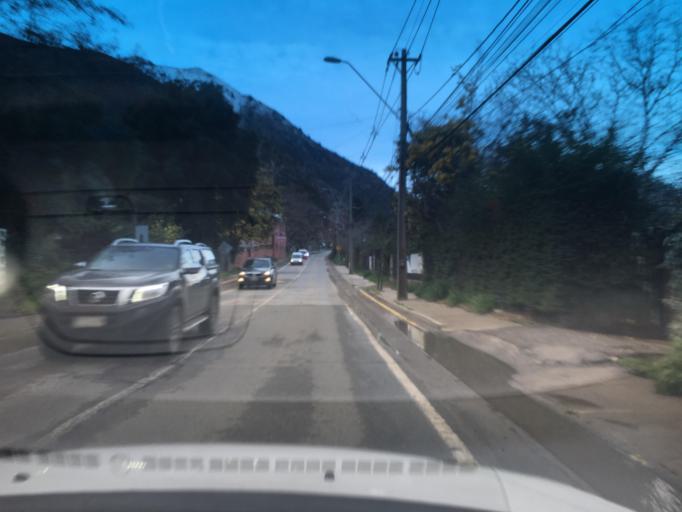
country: CL
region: Santiago Metropolitan
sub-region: Provincia de Cordillera
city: Puente Alto
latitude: -33.5760
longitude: -70.4490
